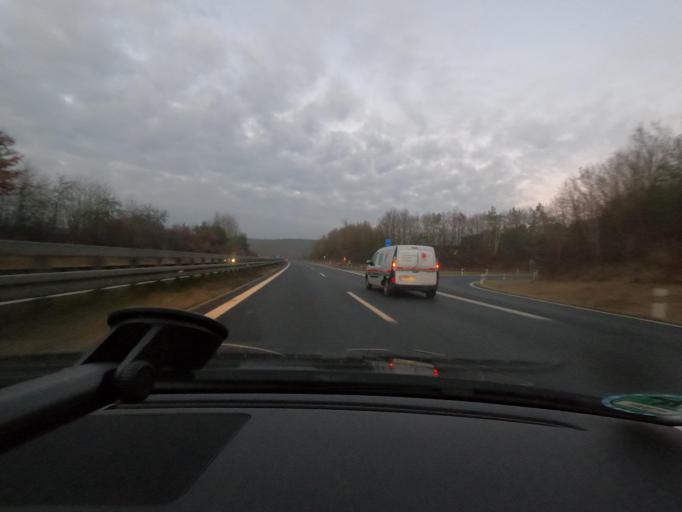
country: DE
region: Bavaria
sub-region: Upper Franconia
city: Zapfendorf
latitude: 50.0131
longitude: 10.9446
